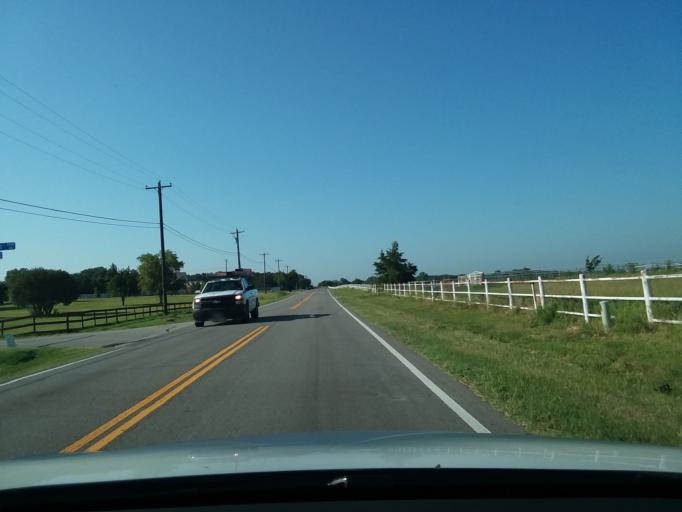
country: US
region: Texas
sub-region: Denton County
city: Bartonville
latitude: 33.0554
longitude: -97.1290
